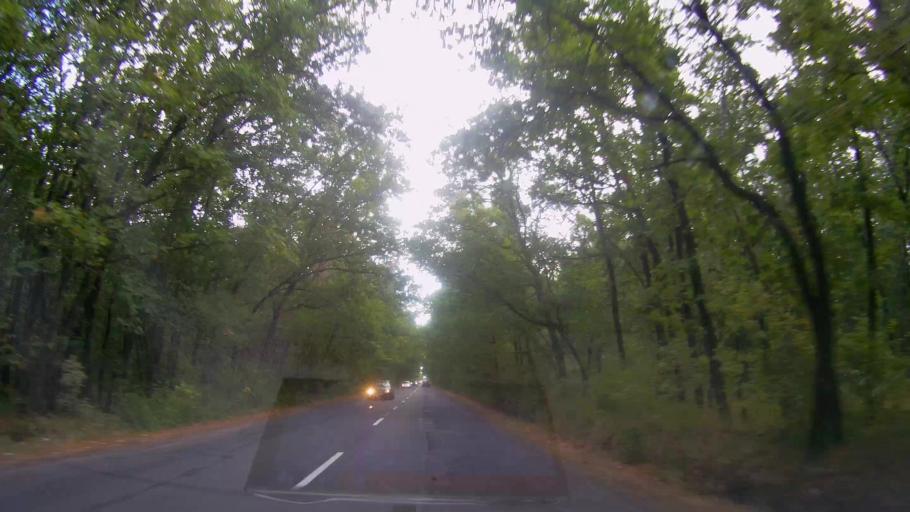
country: BG
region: Burgas
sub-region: Obshtina Primorsko
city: Primorsko
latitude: 42.2804
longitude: 27.7385
